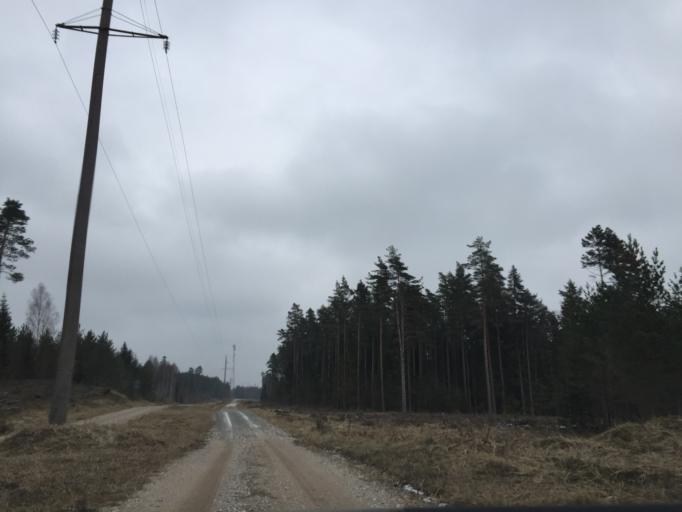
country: EE
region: Saare
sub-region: Kuressaare linn
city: Kuressaare
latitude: 58.3615
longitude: 22.2224
